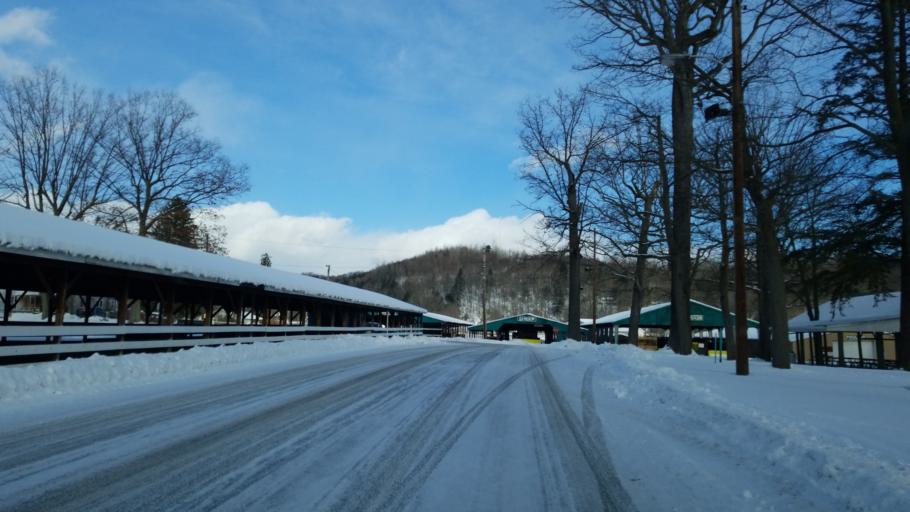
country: US
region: Pennsylvania
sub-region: Clearfield County
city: Clearfield
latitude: 41.0314
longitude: -78.4468
